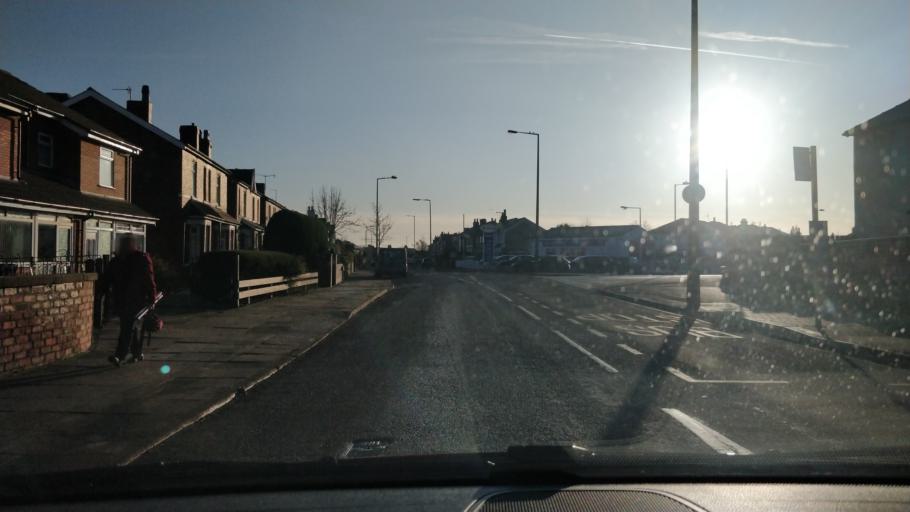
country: GB
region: England
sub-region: Lancashire
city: Banks
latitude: 53.6707
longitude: -2.9484
